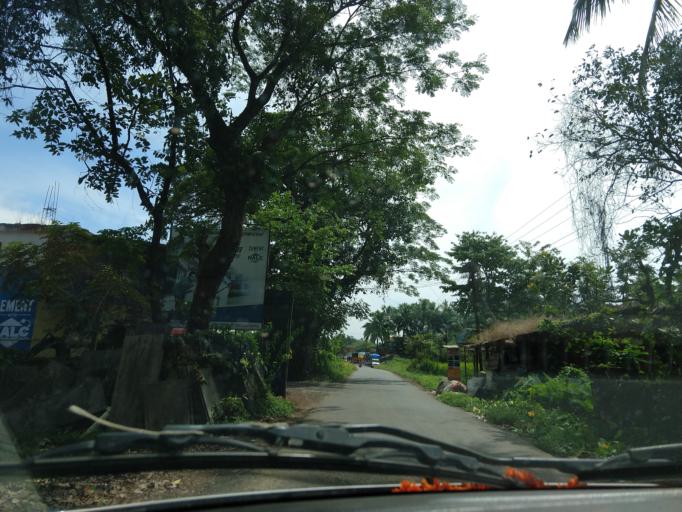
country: IN
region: Maharashtra
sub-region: Sindhudurg
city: Savantvadi
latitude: 15.9705
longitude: 73.7715
